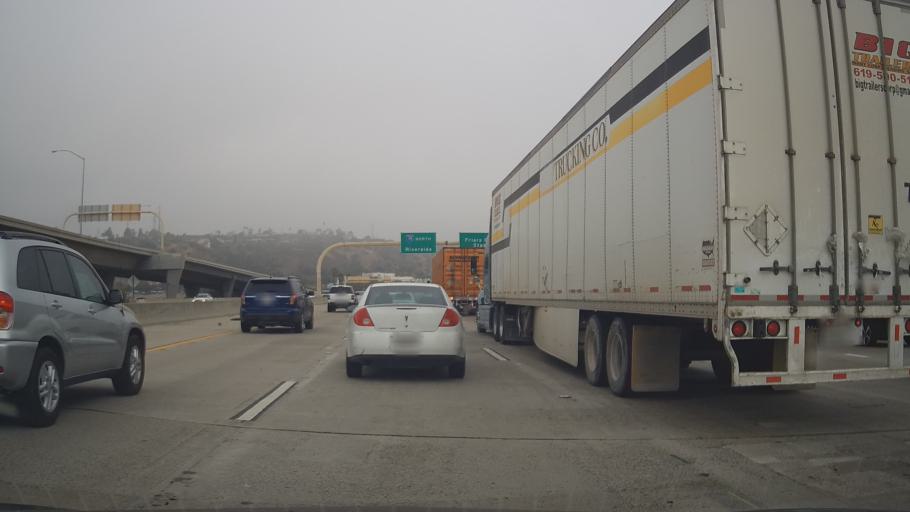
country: US
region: California
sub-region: San Diego County
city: San Diego
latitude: 32.7809
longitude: -117.1126
